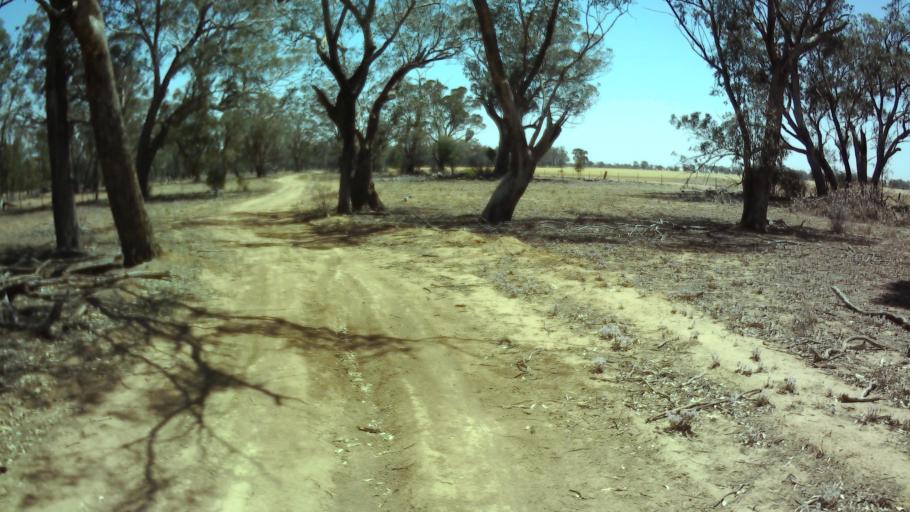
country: AU
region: New South Wales
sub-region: Weddin
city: Grenfell
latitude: -34.0681
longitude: 147.7963
